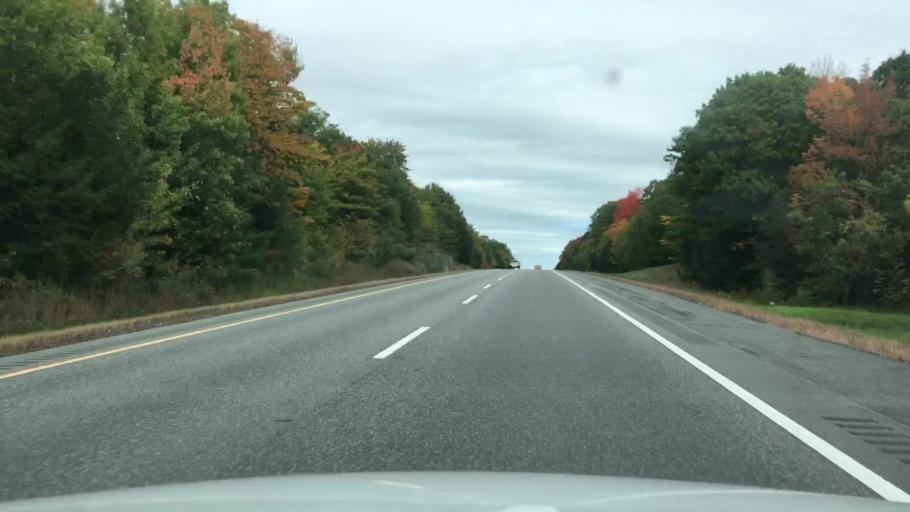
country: US
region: Maine
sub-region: Kennebec County
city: Sidney
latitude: 44.4029
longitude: -69.7511
